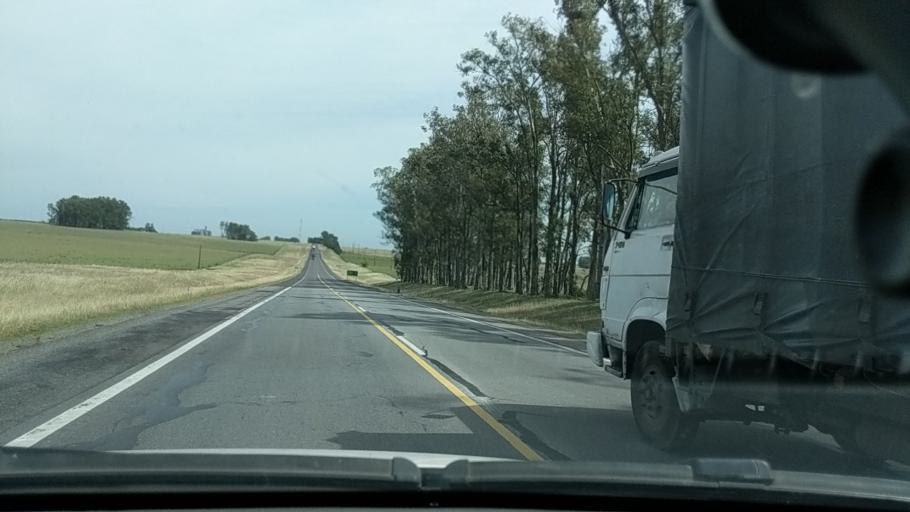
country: UY
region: Durazno
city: Durazno
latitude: -33.5144
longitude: -56.4119
